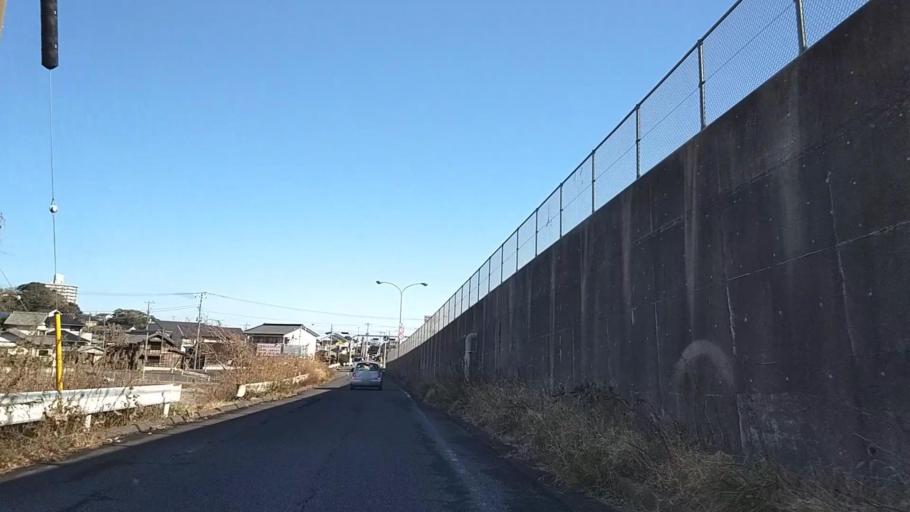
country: JP
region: Chiba
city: Katsuura
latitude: 35.1657
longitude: 140.3289
